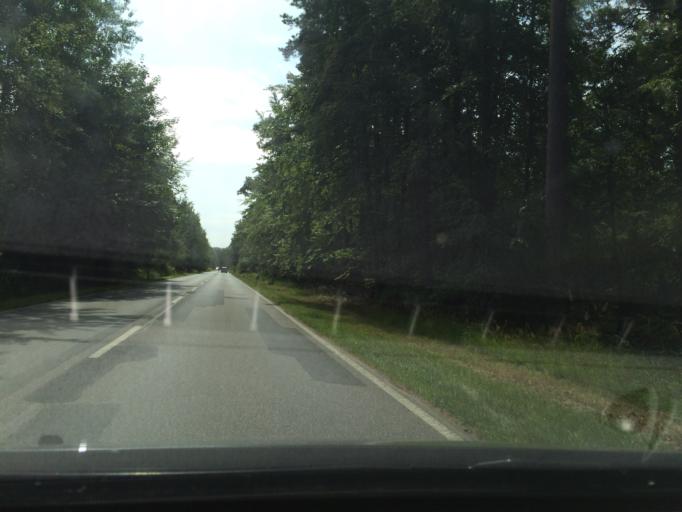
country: DE
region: Mecklenburg-Vorpommern
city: Ostseebad Binz
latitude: 54.4329
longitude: 13.5721
